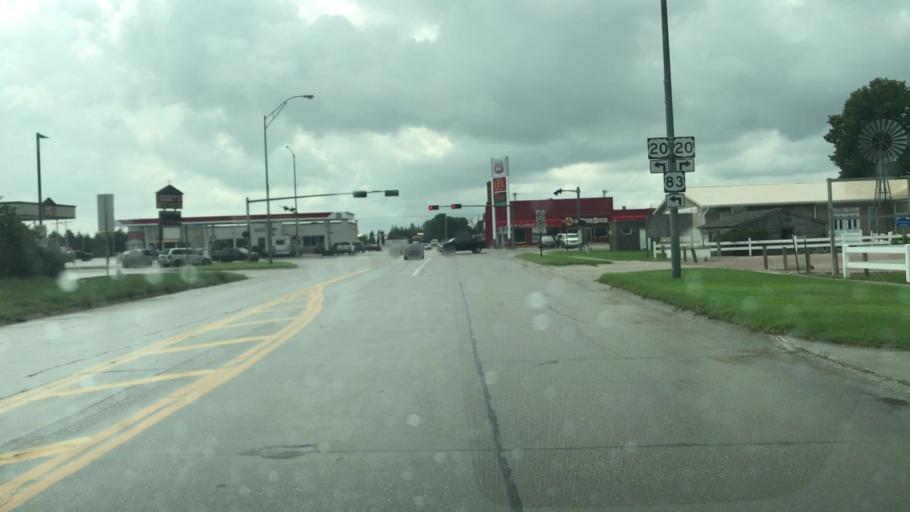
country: US
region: Nebraska
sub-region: Cherry County
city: Valentine
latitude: 42.8687
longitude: -100.5505
